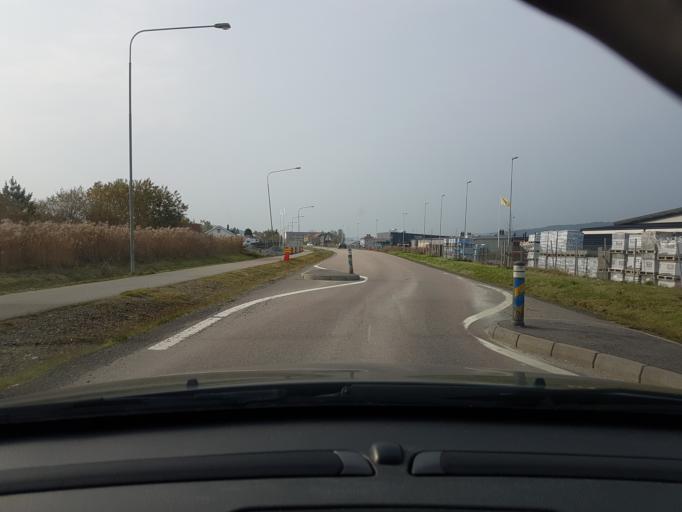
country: SE
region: Vaestra Goetaland
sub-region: Ale Kommun
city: Alvangen
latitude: 57.9635
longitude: 12.1366
